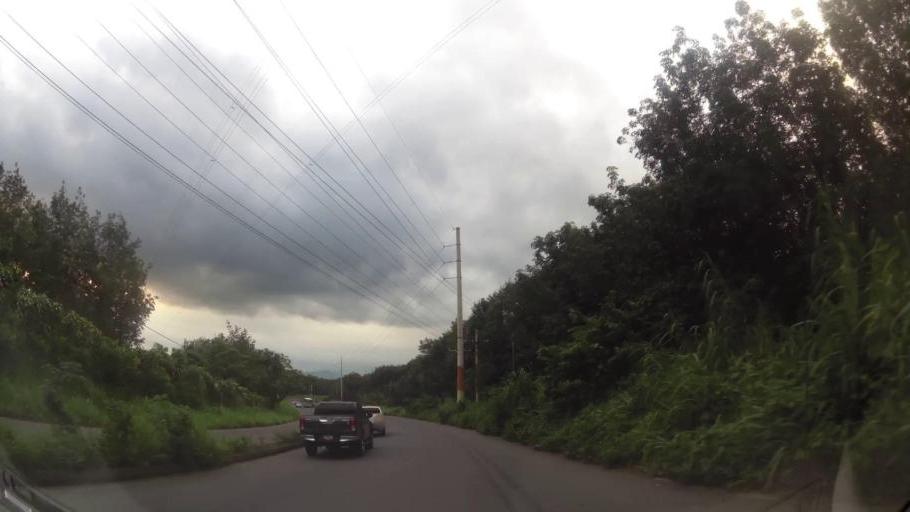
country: GT
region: Escuintla
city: Santa Lucia Cotzumalguapa
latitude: 14.3621
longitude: -91.0971
